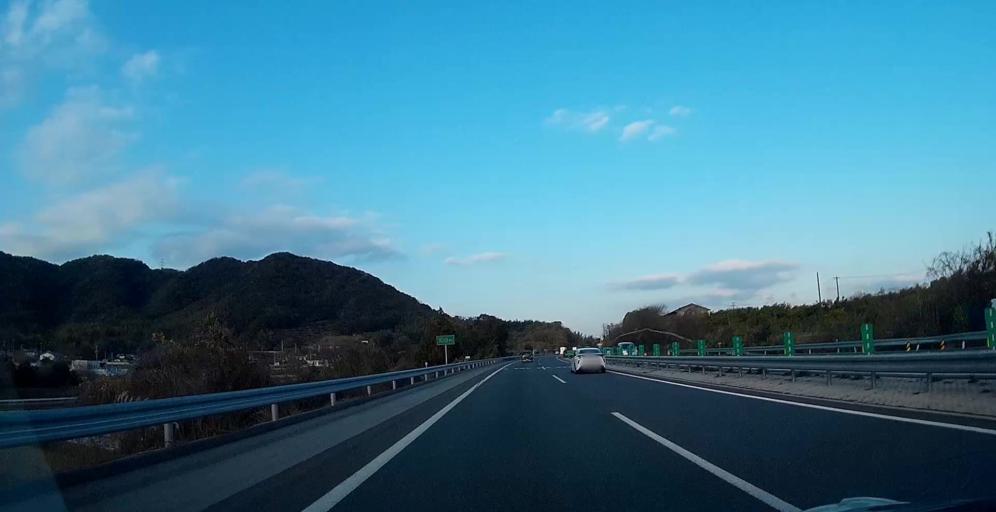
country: JP
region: Kumamoto
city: Uto
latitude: 32.6723
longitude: 130.7165
